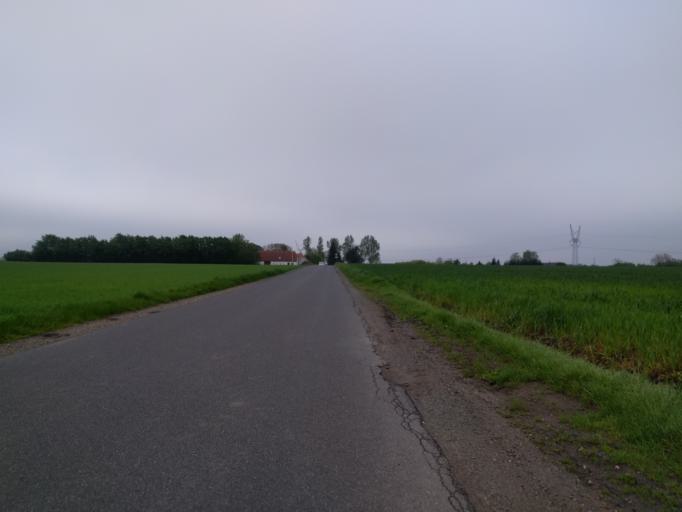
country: DK
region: South Denmark
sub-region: Odense Kommune
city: Bullerup
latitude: 55.3888
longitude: 10.5137
